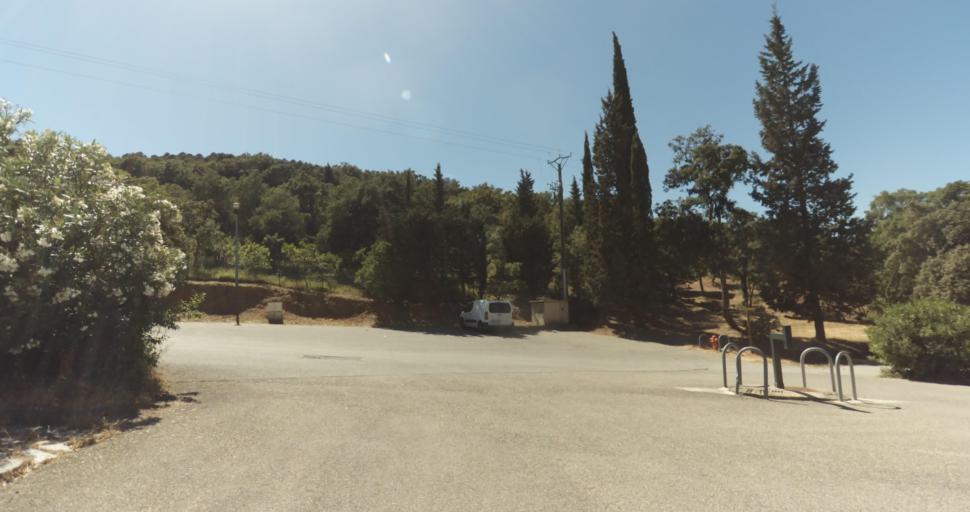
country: FR
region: Provence-Alpes-Cote d'Azur
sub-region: Departement du Var
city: La Croix-Valmer
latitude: 43.2208
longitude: 6.5545
